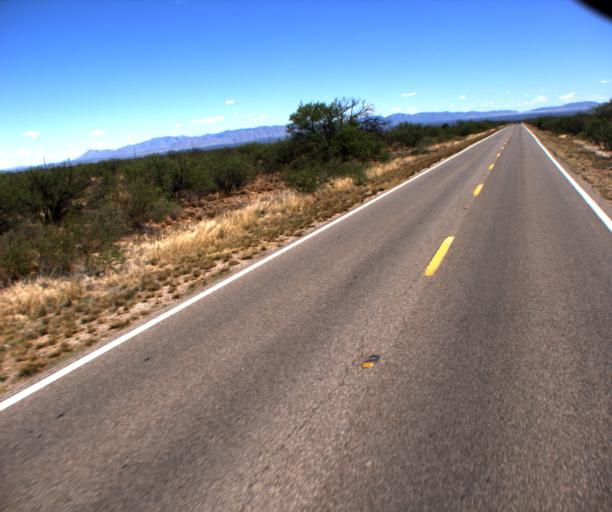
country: US
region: Arizona
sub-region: Cochise County
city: Huachuca City
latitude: 31.7107
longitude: -110.2691
